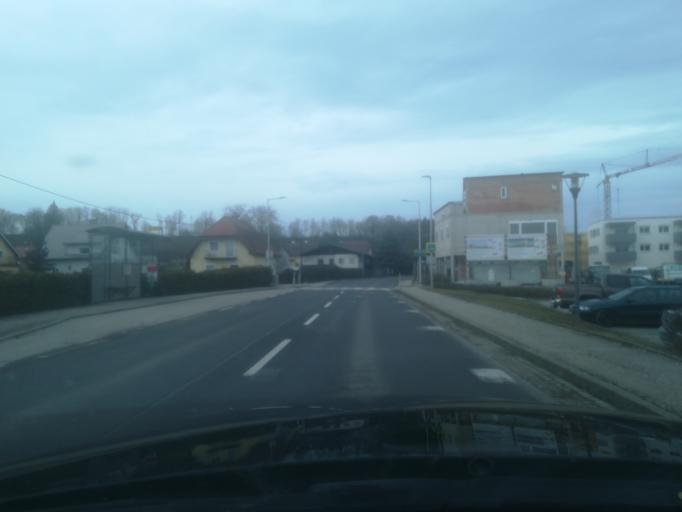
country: AT
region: Upper Austria
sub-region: Wels-Land
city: Lambach
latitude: 48.0947
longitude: 13.8949
